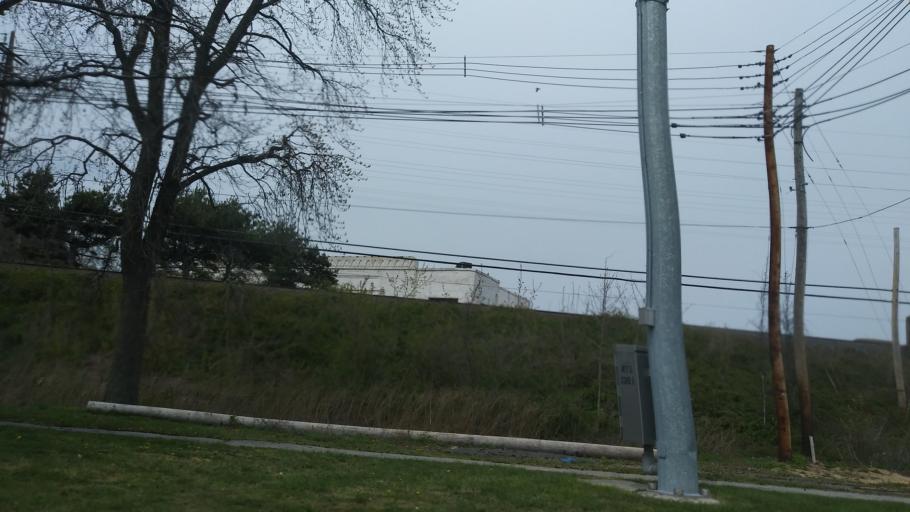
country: US
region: New York
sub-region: Nassau County
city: Rockville Centre
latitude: 40.6573
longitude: -73.6311
